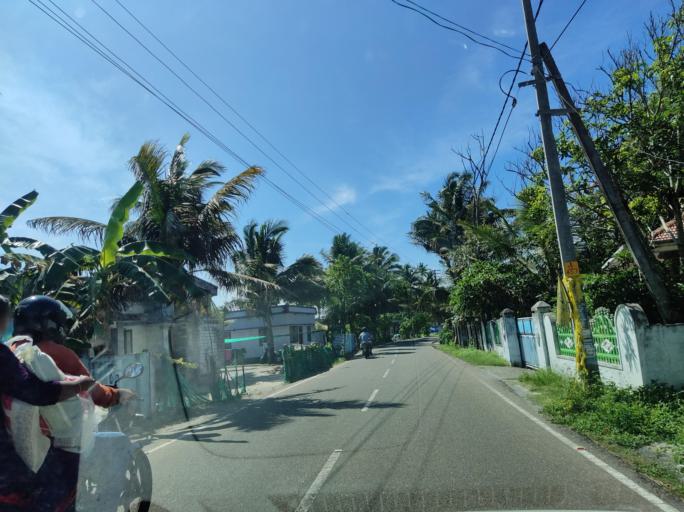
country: IN
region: Kerala
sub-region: Alappuzha
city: Kayankulam
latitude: 9.1843
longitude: 76.4417
